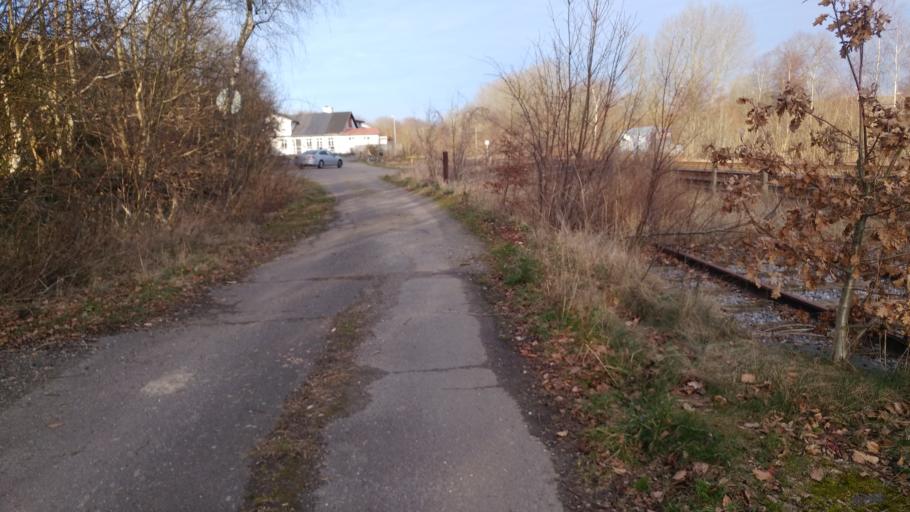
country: DK
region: Central Jutland
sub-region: Arhus Kommune
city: Tranbjerg
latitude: 56.1035
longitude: 10.1021
